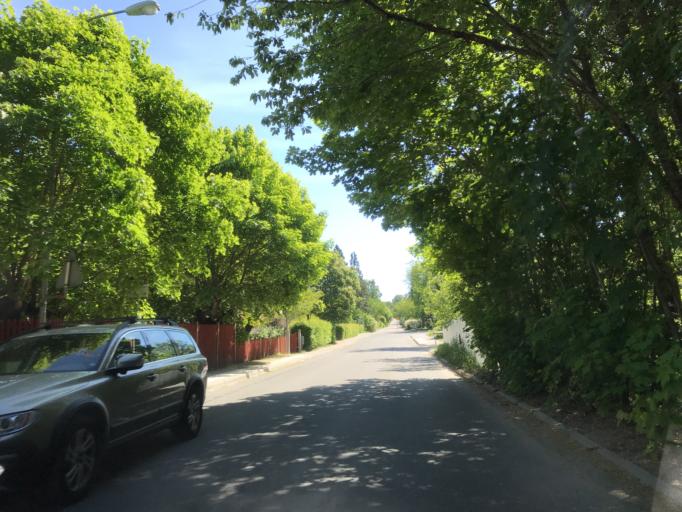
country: SE
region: Stockholm
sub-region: Sollentuna Kommun
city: Sollentuna
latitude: 59.4262
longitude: 17.9561
